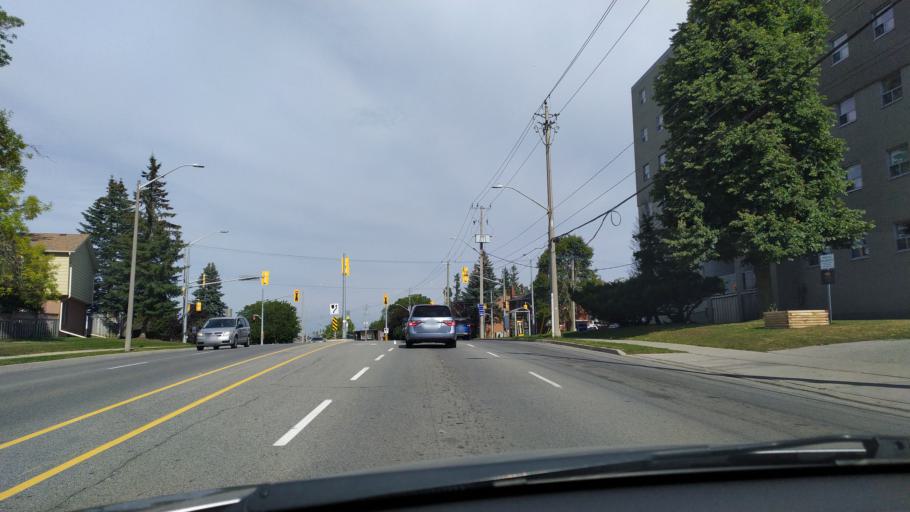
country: CA
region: Ontario
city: Kitchener
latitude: 43.4328
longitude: -80.5099
